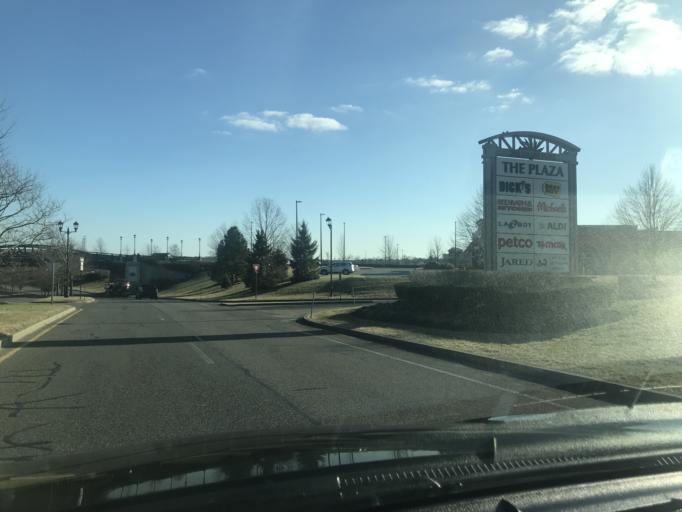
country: US
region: Massachusetts
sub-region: Plymouth County
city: North Plymouth
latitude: 41.9536
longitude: -70.7151
